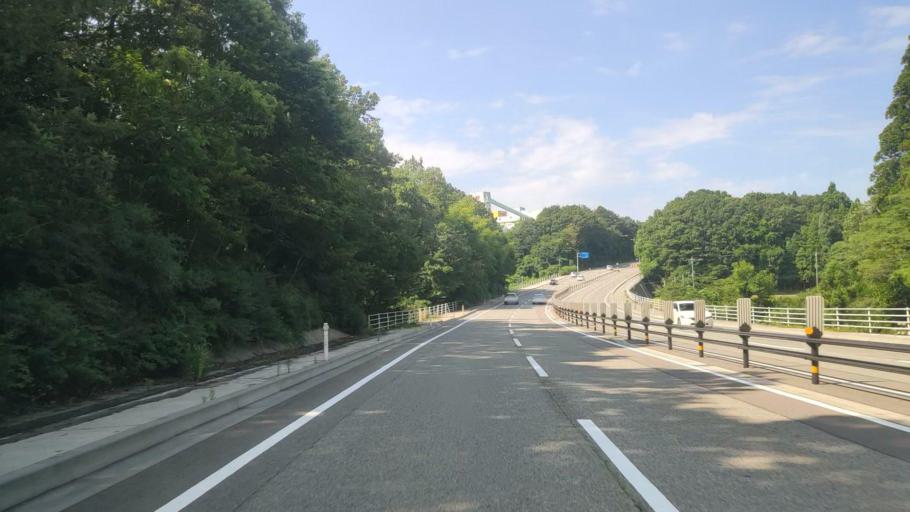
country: JP
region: Ishikawa
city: Komatsu
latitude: 36.4215
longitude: 136.5286
